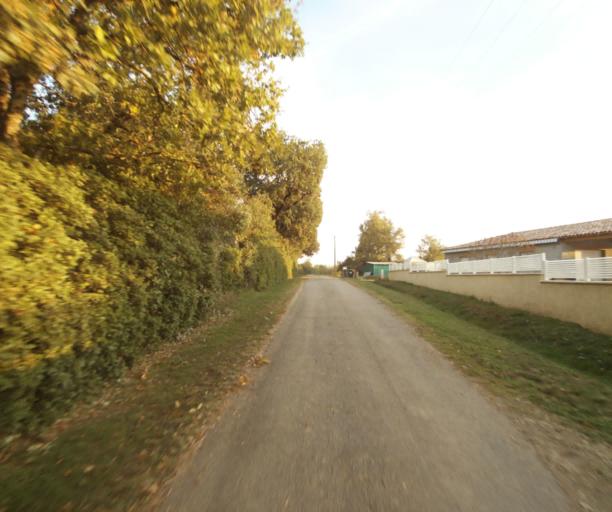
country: FR
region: Midi-Pyrenees
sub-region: Departement du Tarn-et-Garonne
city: Pompignan
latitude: 43.8296
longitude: 1.3181
